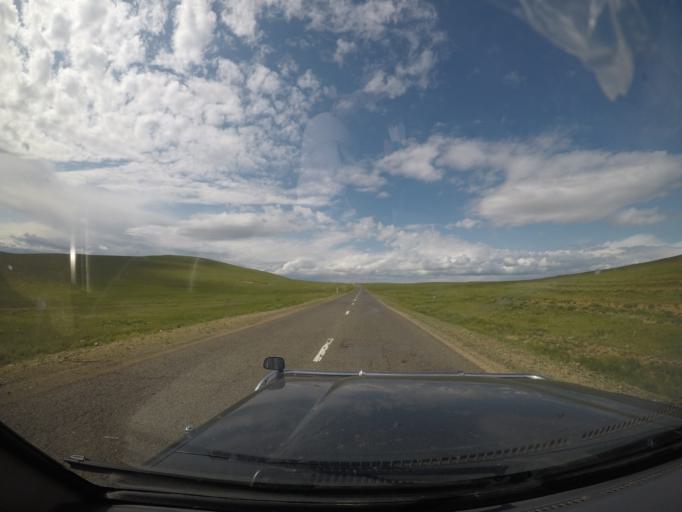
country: MN
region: Hentiy
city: Modot
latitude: 47.5792
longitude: 109.2996
